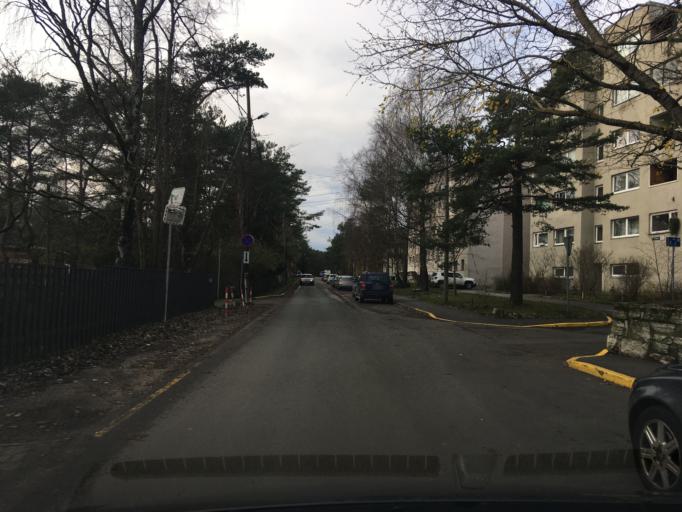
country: EE
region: Harju
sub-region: Tallinna linn
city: Tallinn
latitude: 59.3747
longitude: 24.7098
